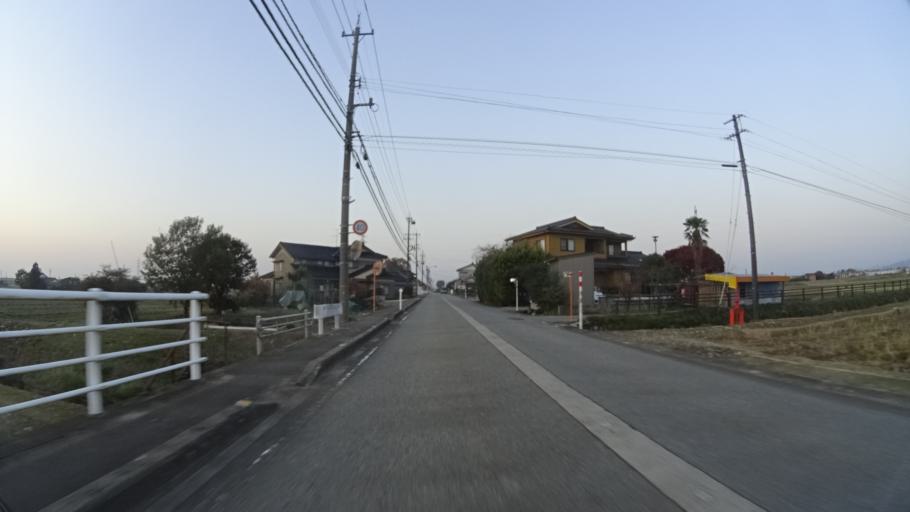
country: JP
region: Toyama
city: Namerikawa
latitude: 36.7504
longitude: 137.3734
